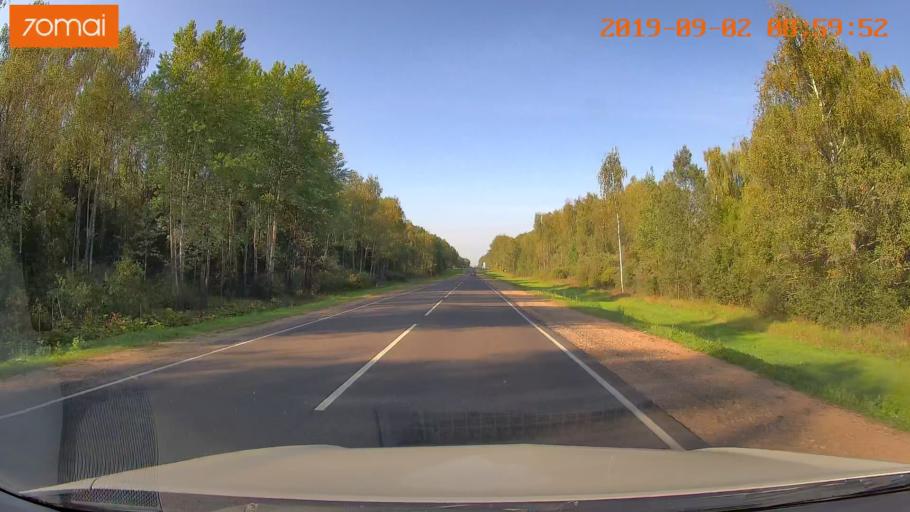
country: RU
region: Kaluga
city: Myatlevo
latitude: 54.9174
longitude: 35.7206
